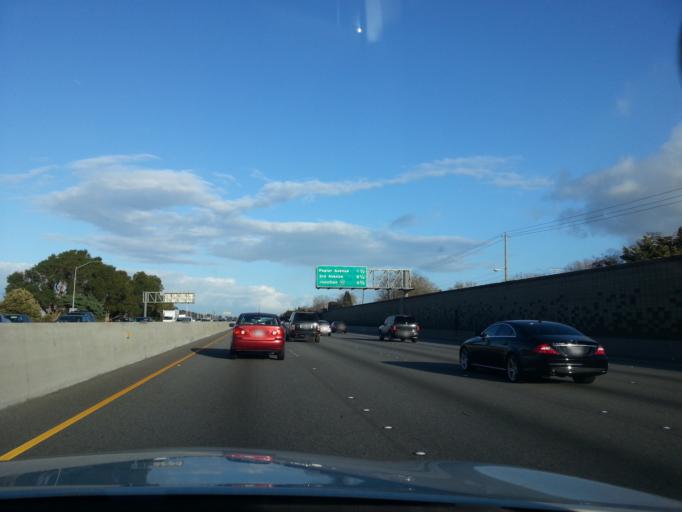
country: US
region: California
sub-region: San Mateo County
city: Burlingame
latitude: 37.5871
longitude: -122.3502
